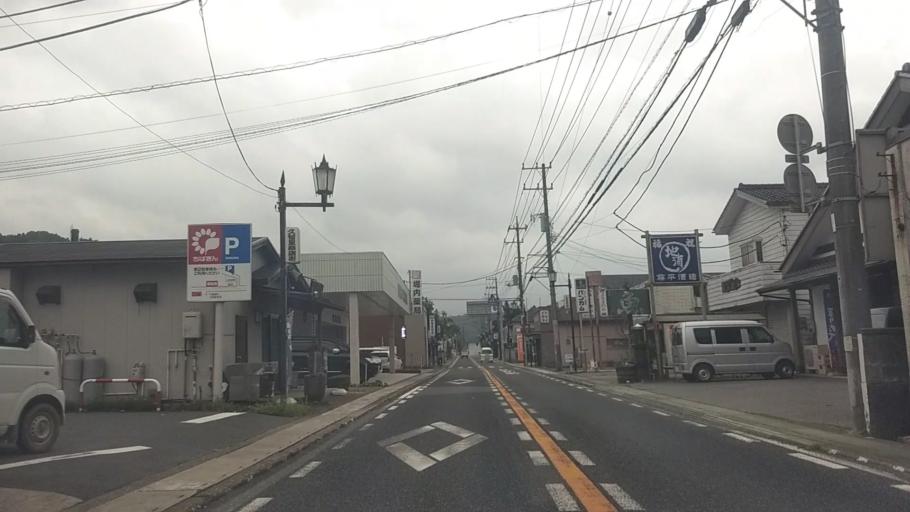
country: JP
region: Chiba
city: Kisarazu
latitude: 35.2954
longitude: 140.0777
